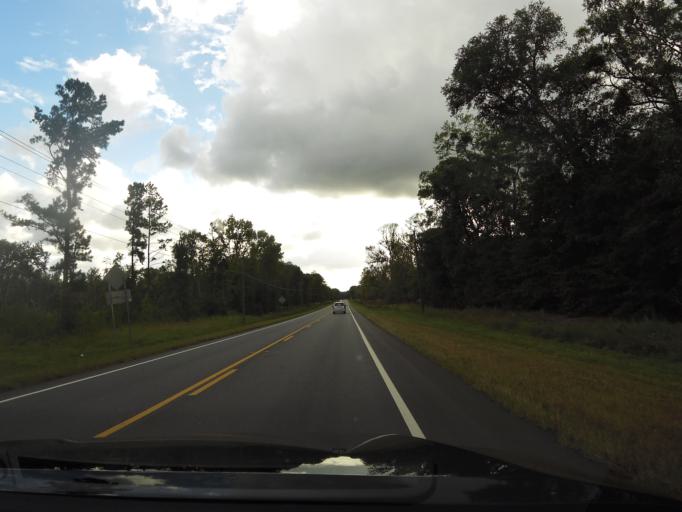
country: US
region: Georgia
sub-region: Liberty County
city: Midway
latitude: 31.8383
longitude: -81.4149
